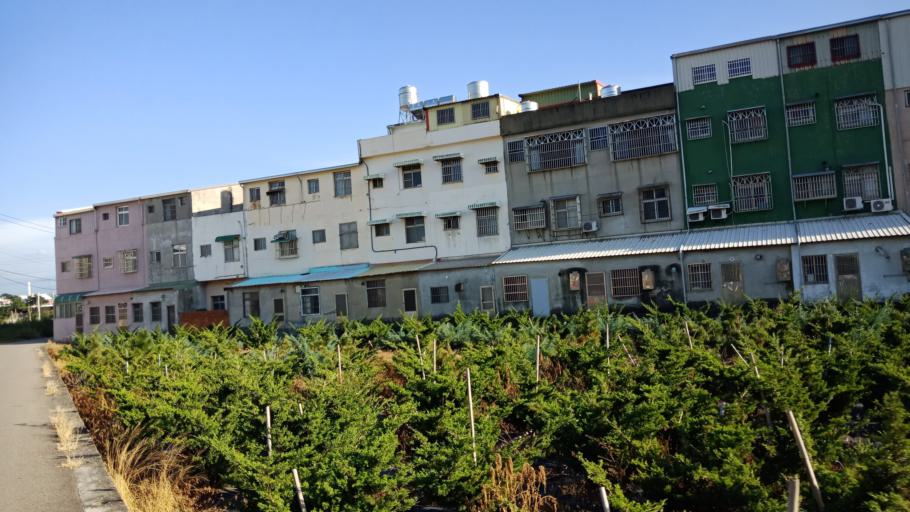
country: TW
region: Taiwan
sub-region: Miaoli
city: Miaoli
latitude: 24.4923
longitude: 120.6876
